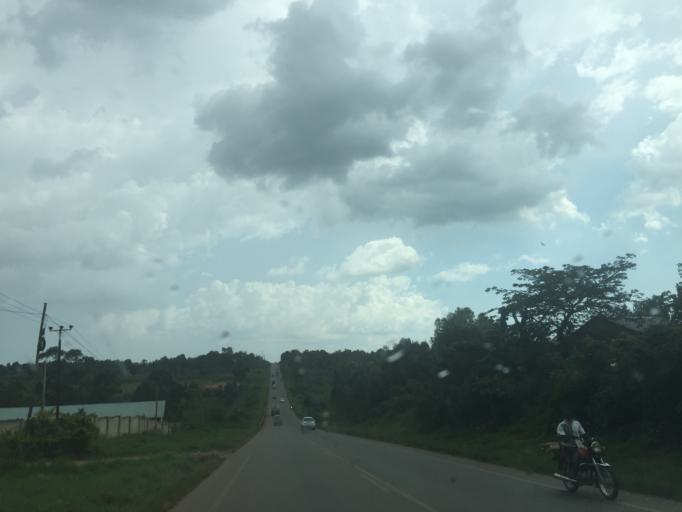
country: UG
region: Central Region
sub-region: Luwero District
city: Wobulenzi
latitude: 0.6045
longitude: 32.5322
